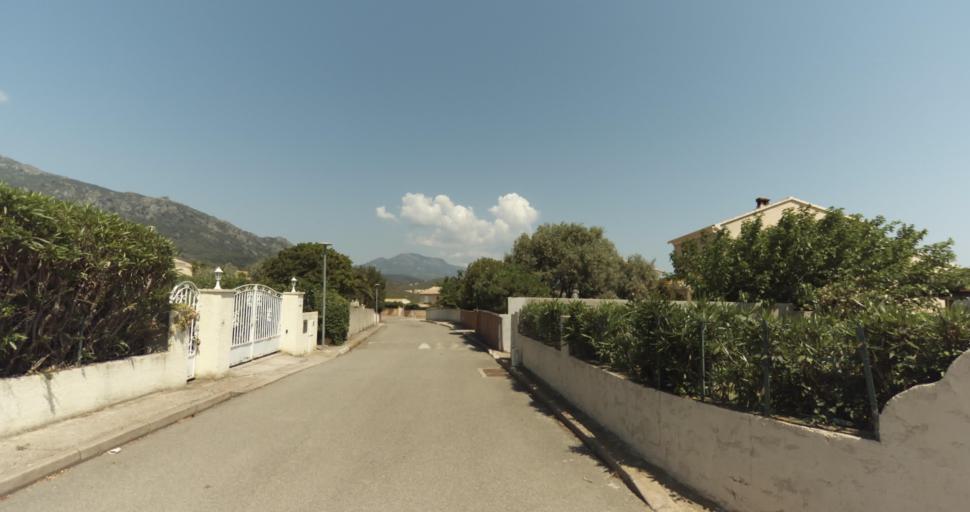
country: FR
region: Corsica
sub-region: Departement de la Haute-Corse
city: Biguglia
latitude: 42.6057
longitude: 9.4314
